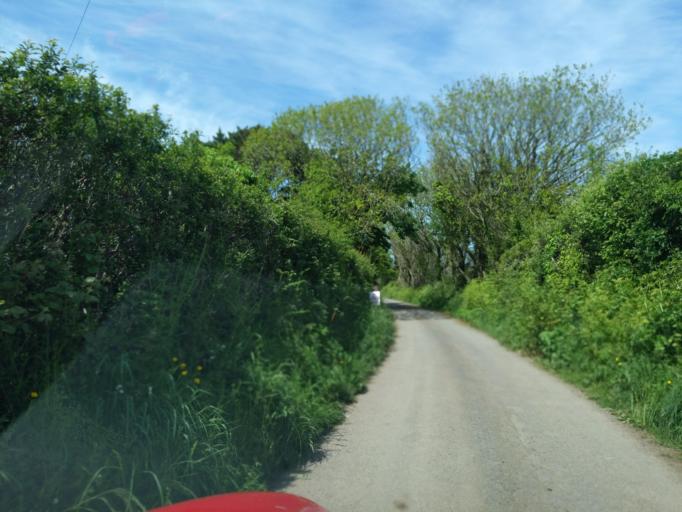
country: GB
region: England
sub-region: Borough of Torbay
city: Brixham
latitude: 50.3615
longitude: -3.5310
